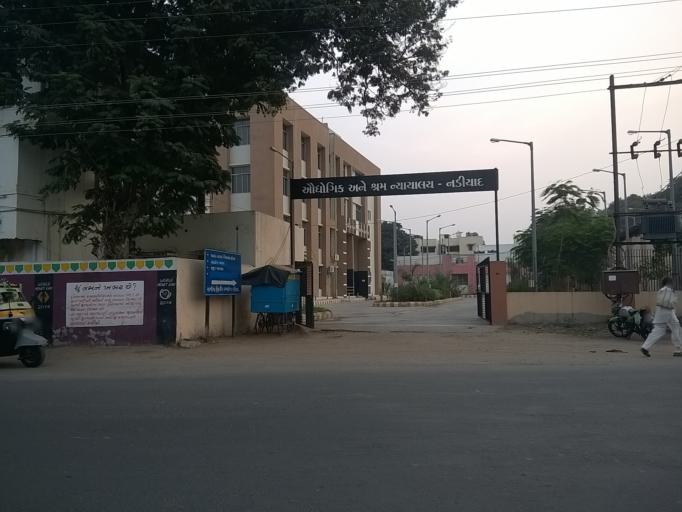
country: IN
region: Gujarat
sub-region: Kheda
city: Nadiad
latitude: 22.6965
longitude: 72.8577
